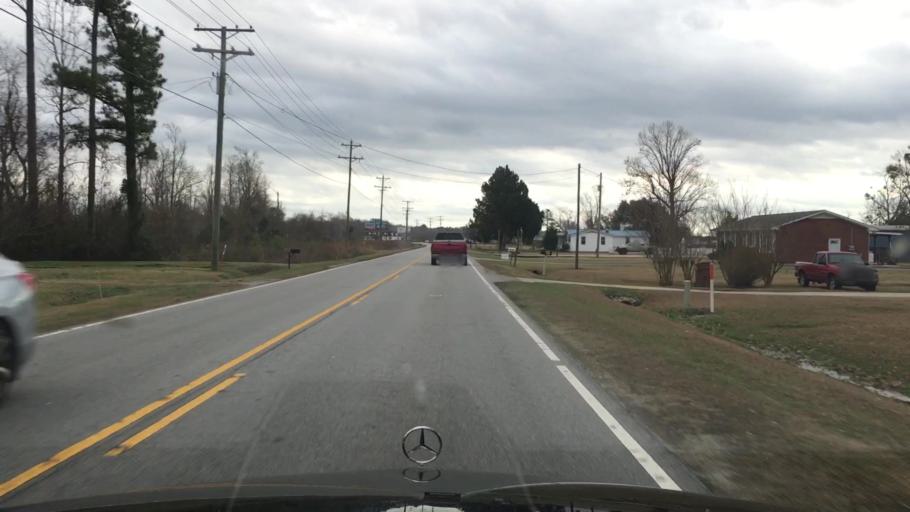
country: US
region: North Carolina
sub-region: Onslow County
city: Half Moon
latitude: 34.8500
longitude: -77.4817
